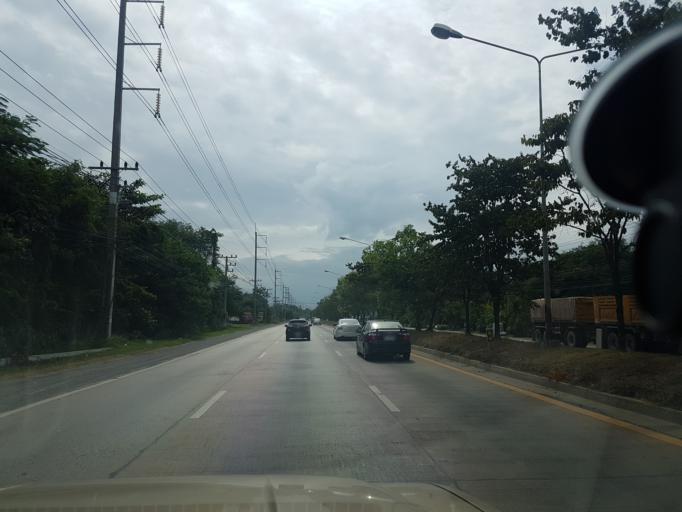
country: TH
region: Sara Buri
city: Phra Phutthabat
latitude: 14.7142
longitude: 100.8214
